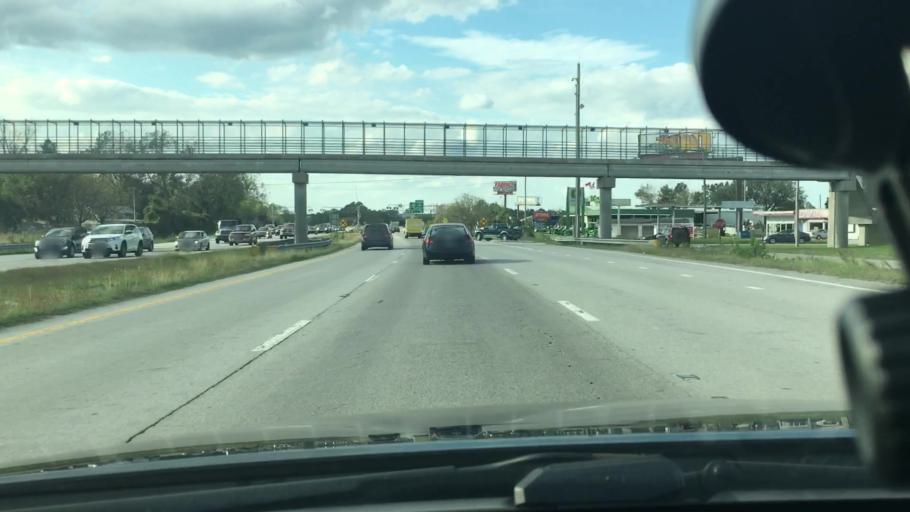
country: US
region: North Carolina
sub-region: Craven County
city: James City
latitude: 35.0869
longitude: -77.0333
